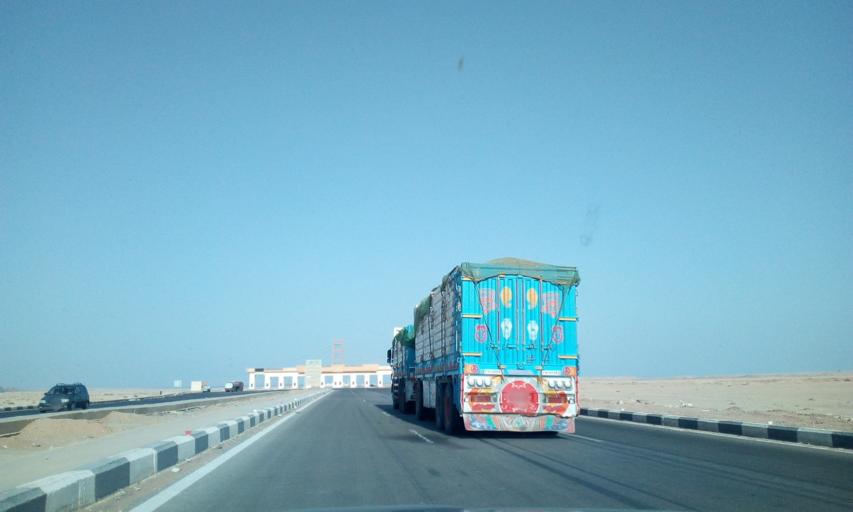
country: EG
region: As Suways
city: Ain Sukhna
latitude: 29.1104
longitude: 32.5461
